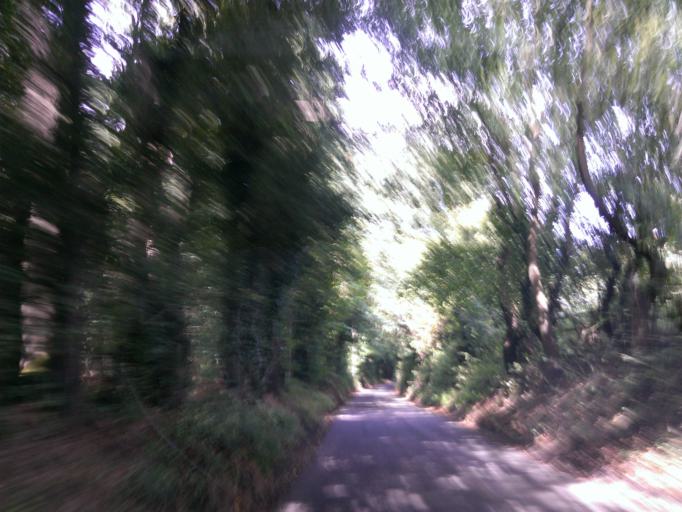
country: GB
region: England
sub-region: Essex
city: Sible Hedingham
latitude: 51.9658
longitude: 0.6248
